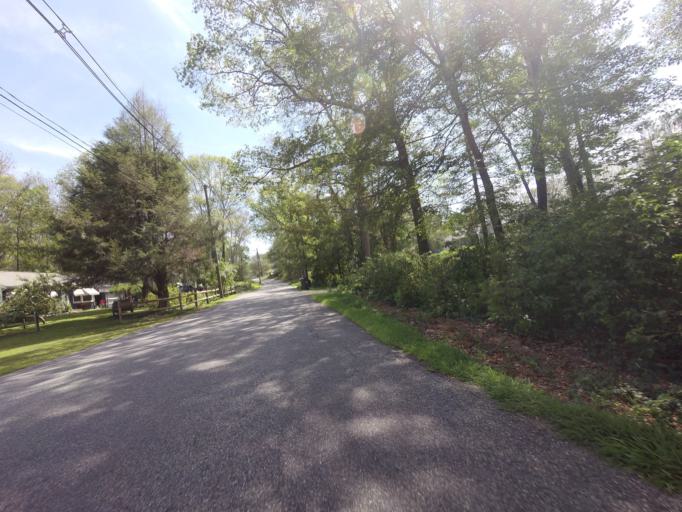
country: US
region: Connecticut
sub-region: Windham County
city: East Brooklyn
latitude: 41.8229
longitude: -71.9299
